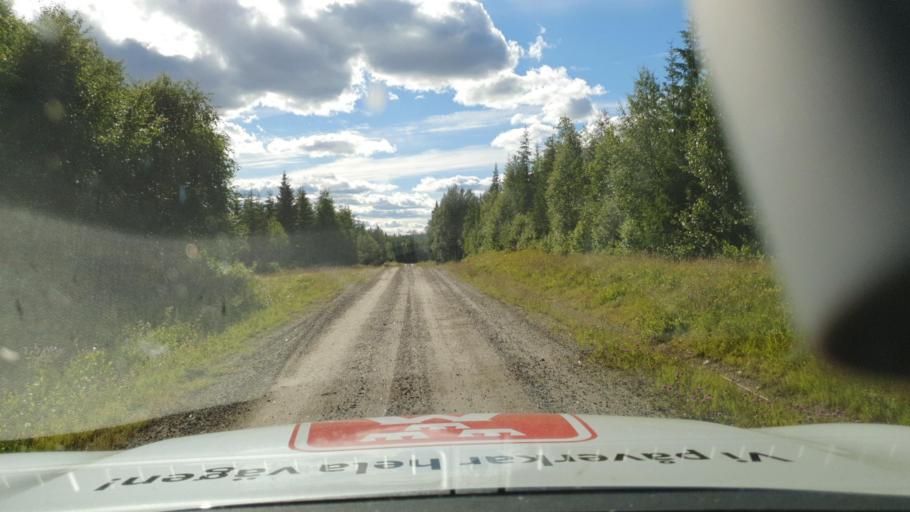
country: SE
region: Vaesterbotten
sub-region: Lycksele Kommun
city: Lycksele
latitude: 64.4028
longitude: 18.3111
